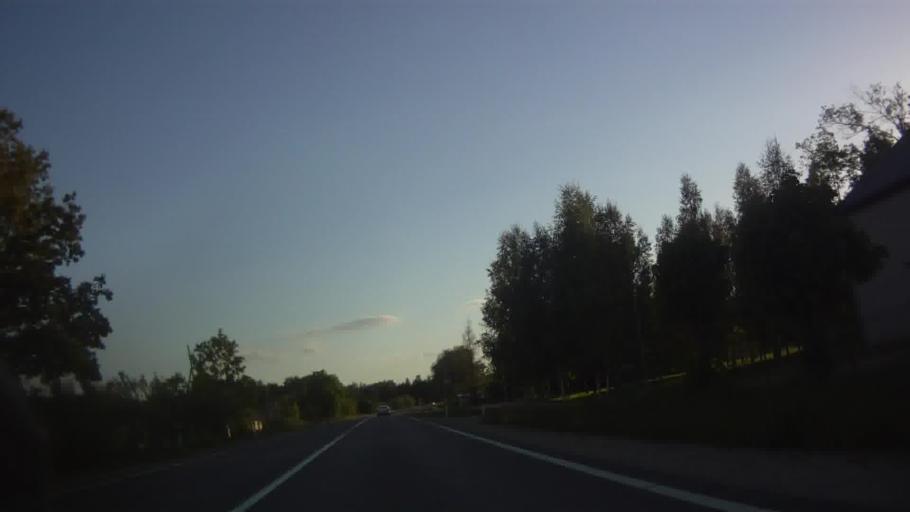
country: LV
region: Livani
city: Livani
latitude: 56.5444
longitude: 26.0970
